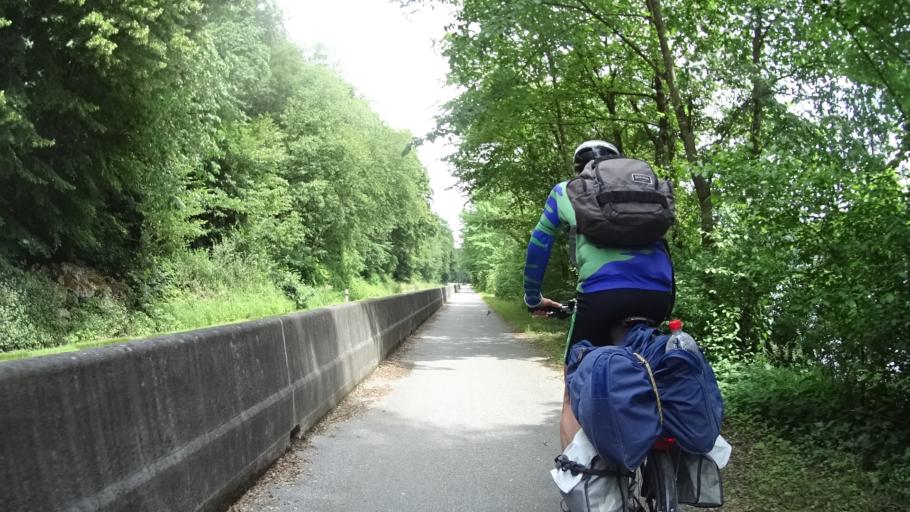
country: DE
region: Bavaria
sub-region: Lower Bavaria
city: Aicha vorm Wald
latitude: 48.6099
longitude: 13.3005
